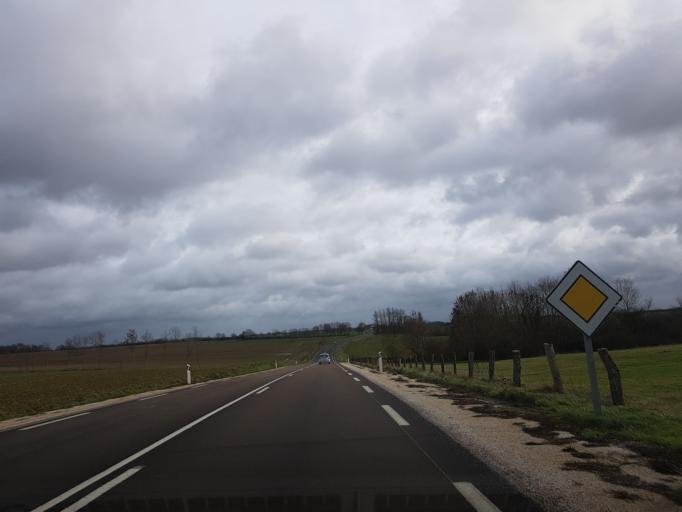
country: FR
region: Champagne-Ardenne
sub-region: Departement de la Haute-Marne
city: Chalindrey
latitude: 47.8539
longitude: 5.4013
